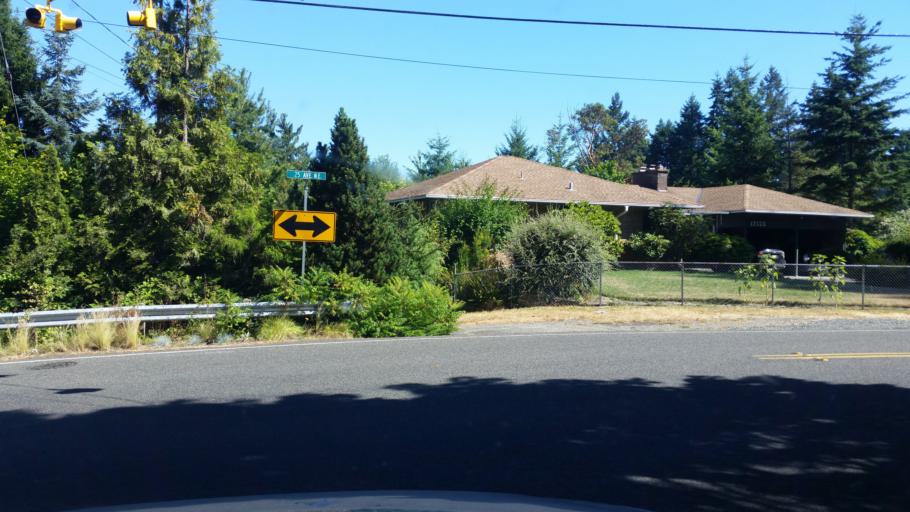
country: US
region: Washington
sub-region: King County
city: Lake Forest Park
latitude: 47.7531
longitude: -122.3026
